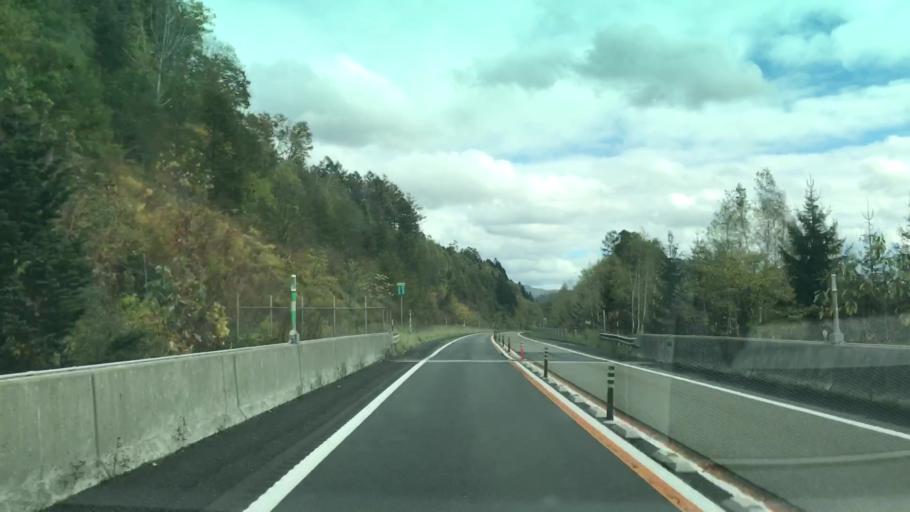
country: JP
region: Hokkaido
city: Chitose
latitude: 42.9137
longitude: 141.9737
